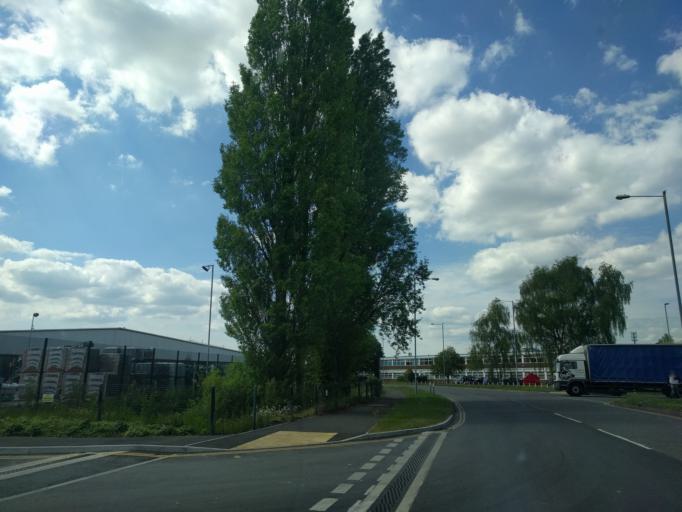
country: GB
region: England
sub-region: Borough of Swindon
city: Swindon
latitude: 51.5753
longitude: -1.7676
